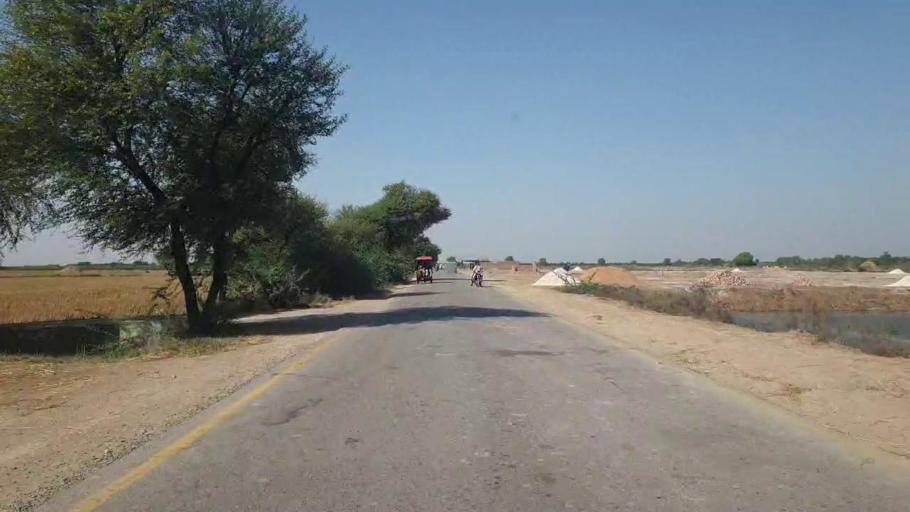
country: PK
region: Sindh
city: Rajo Khanani
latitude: 25.0083
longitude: 68.8353
